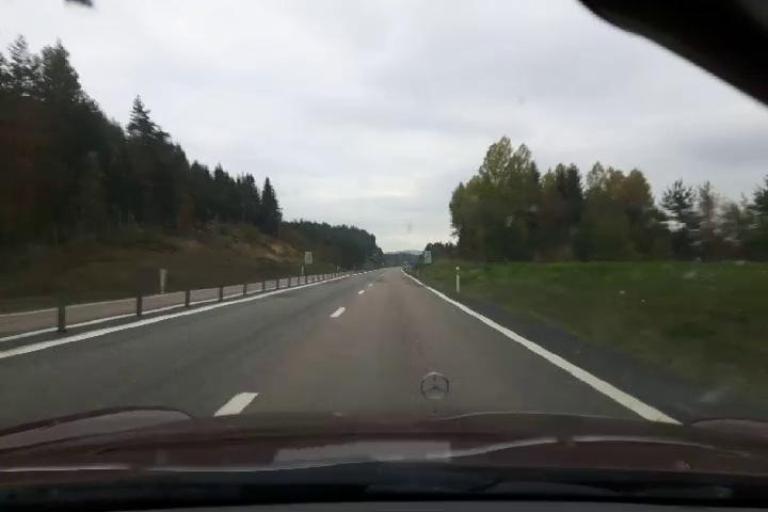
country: SE
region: Vaesternorrland
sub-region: Kramfors Kommun
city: Nordingra
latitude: 62.9283
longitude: 18.0974
